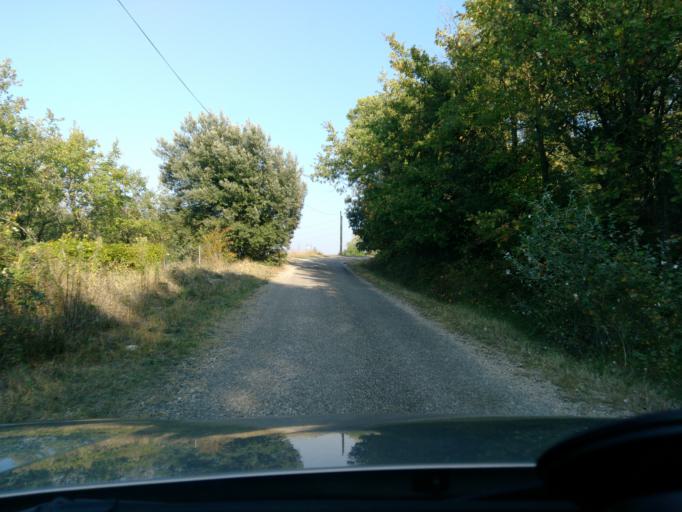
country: FR
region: Rhone-Alpes
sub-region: Departement de la Drome
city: Montboucher-sur-Jabron
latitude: 44.5369
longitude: 4.8218
